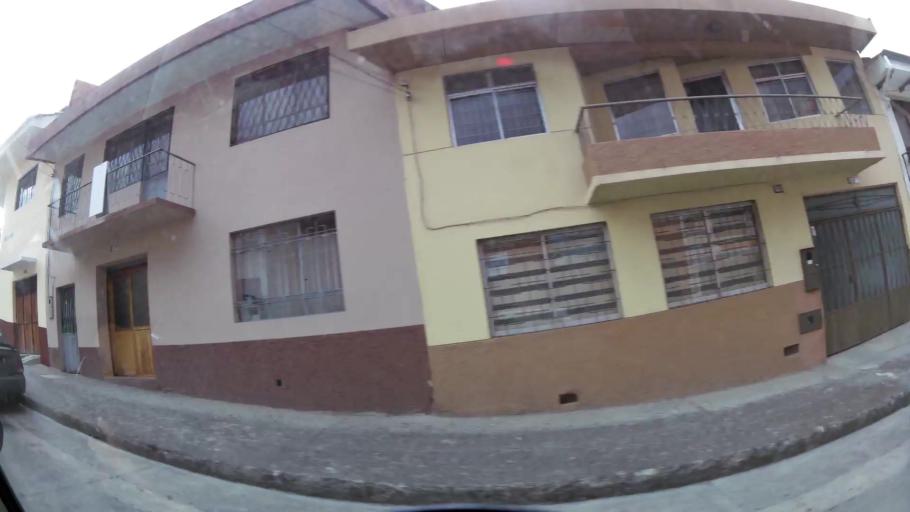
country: EC
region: Azuay
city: Cuenca
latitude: -2.8903
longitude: -79.0155
